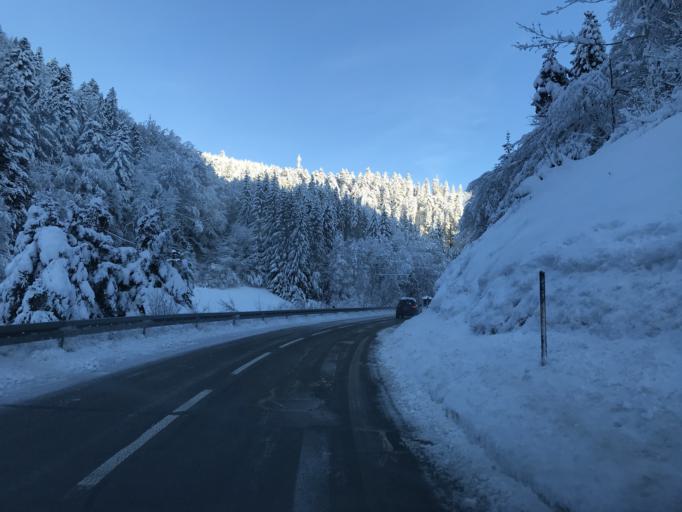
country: DE
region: Baden-Wuerttemberg
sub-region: Freiburg Region
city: Zell im Wiesental
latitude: 47.7482
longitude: 7.8233
